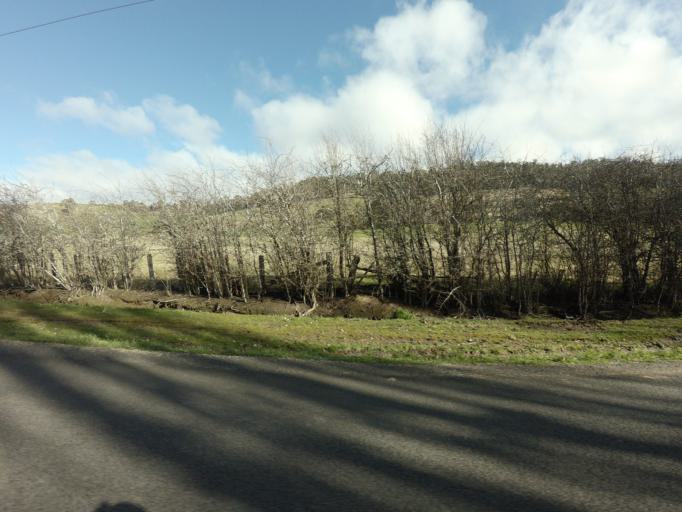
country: AU
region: Tasmania
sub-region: Derwent Valley
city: New Norfolk
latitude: -42.6116
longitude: 146.7116
